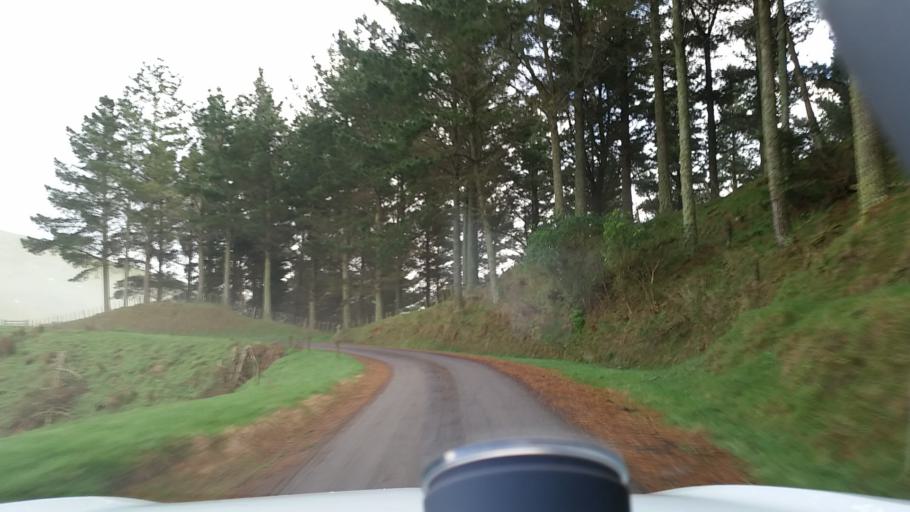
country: NZ
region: Taranaki
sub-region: South Taranaki District
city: Eltham
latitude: -39.4371
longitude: 174.4505
